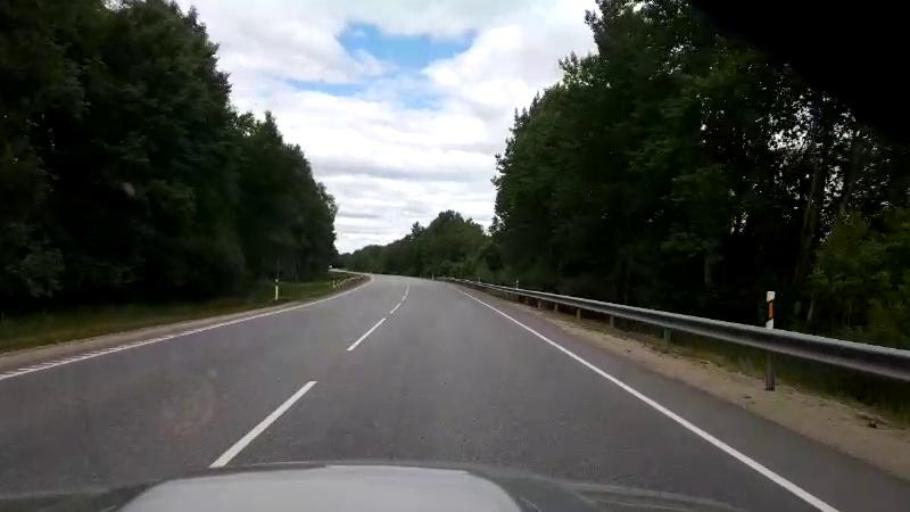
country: EE
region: Raplamaa
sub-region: Maerjamaa vald
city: Marjamaa
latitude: 58.9465
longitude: 24.4679
